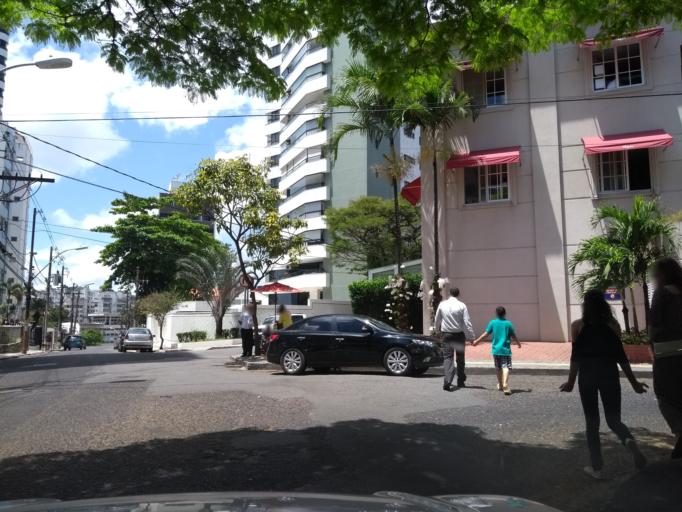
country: BR
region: Bahia
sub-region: Salvador
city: Salvador
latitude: -12.9975
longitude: -38.5221
